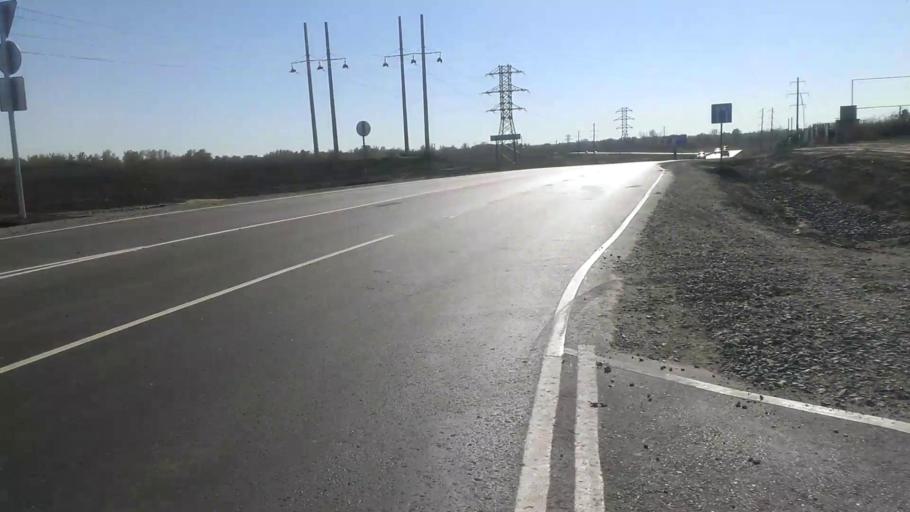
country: RU
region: Altai Krai
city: Sannikovo
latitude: 53.3364
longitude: 83.9385
